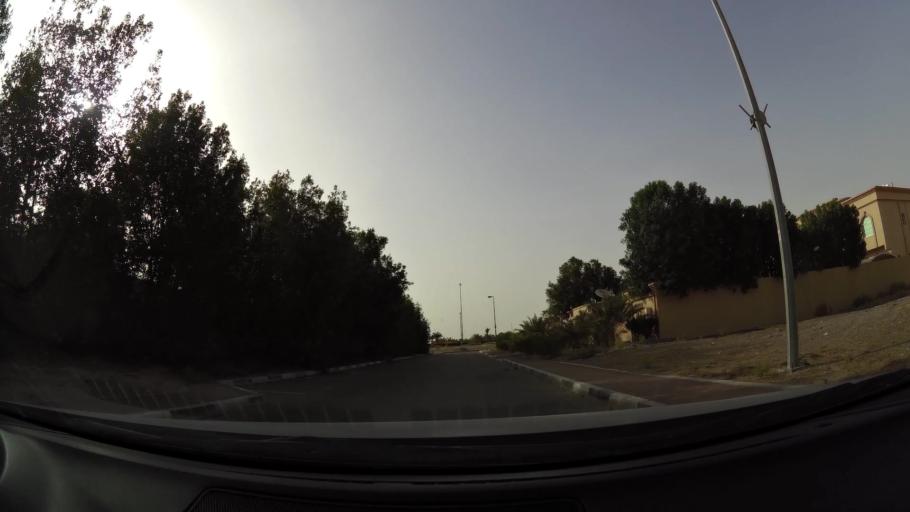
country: AE
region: Abu Dhabi
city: Al Ain
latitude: 24.2213
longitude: 55.6505
